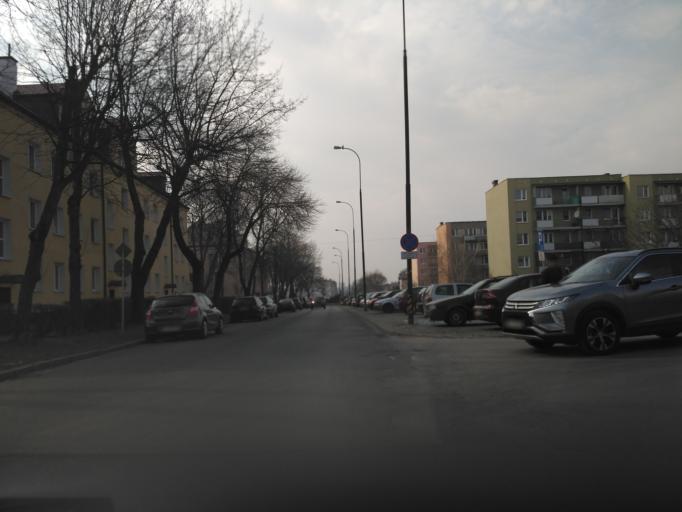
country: PL
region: Lublin Voivodeship
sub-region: Powiat lubelski
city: Lublin
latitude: 51.2351
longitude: 22.5911
